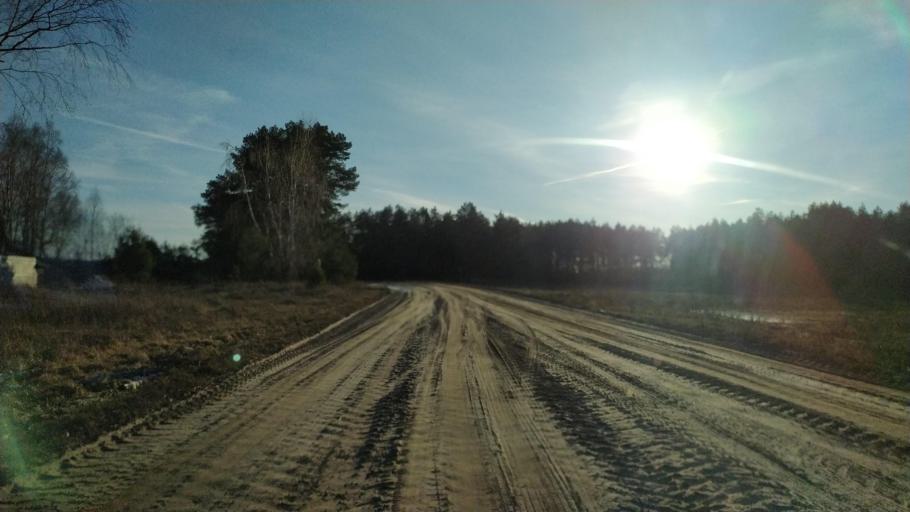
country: BY
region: Brest
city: Pruzhany
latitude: 52.5502
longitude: 24.2869
